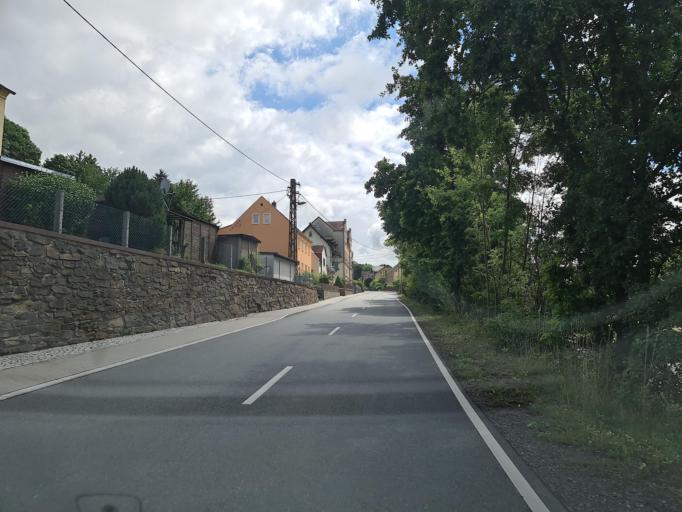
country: DE
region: Saxony
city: Leubsdorf
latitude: 50.8028
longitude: 13.1409
